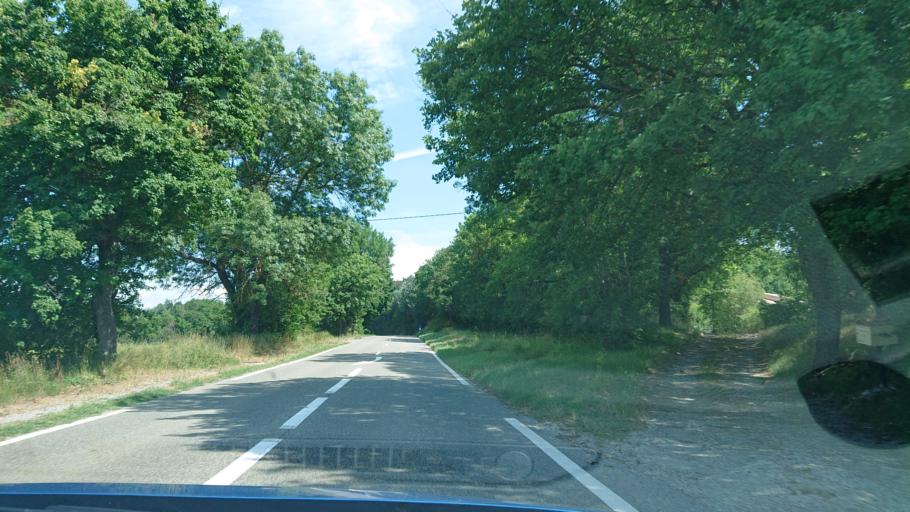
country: FR
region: Provence-Alpes-Cote d'Azur
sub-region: Departement des Alpes-de-Haute-Provence
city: Sisteron
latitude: 44.2134
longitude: 5.9403
